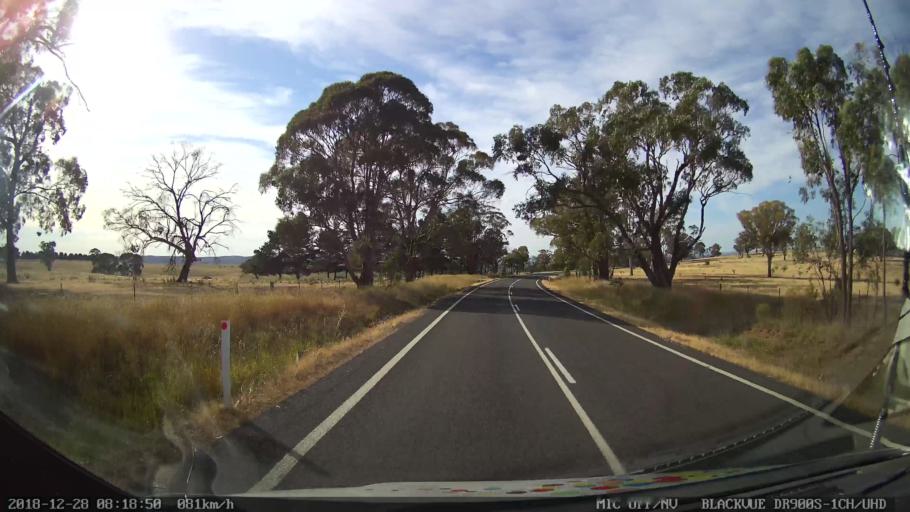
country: AU
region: New South Wales
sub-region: Blayney
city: Blayney
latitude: -33.8514
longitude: 149.3508
